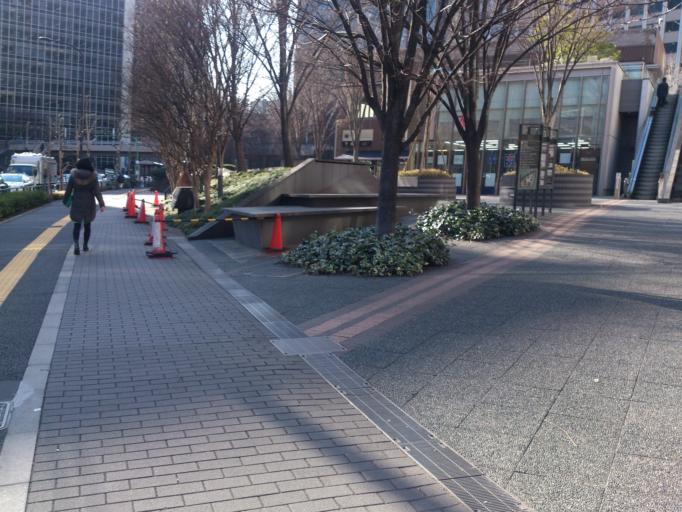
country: JP
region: Tokyo
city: Tokyo
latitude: 35.6708
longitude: 139.7487
